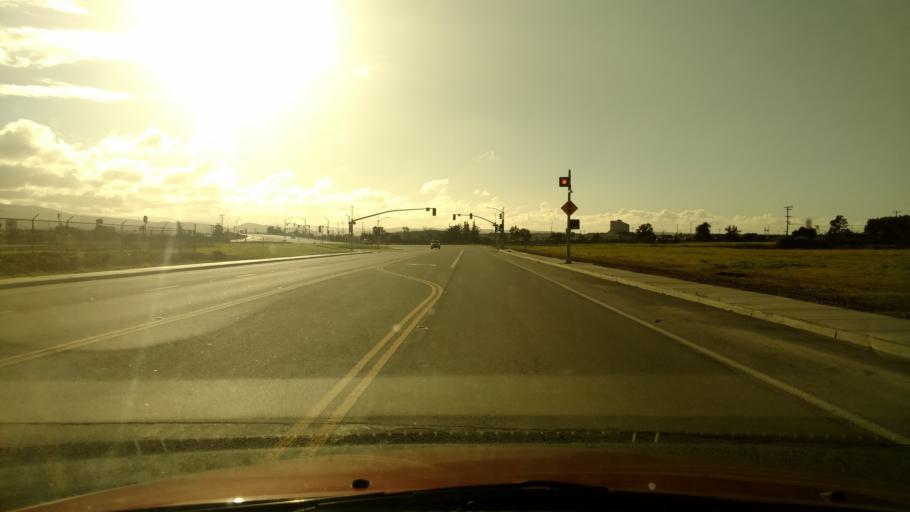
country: US
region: California
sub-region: Monterey County
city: Salinas
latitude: 36.6642
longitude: -121.6192
